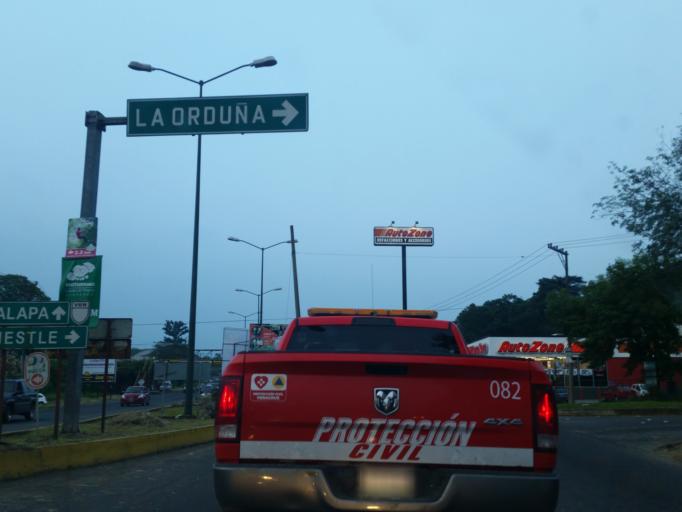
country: MX
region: Veracruz
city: Coatepec
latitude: 19.4681
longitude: -96.9455
